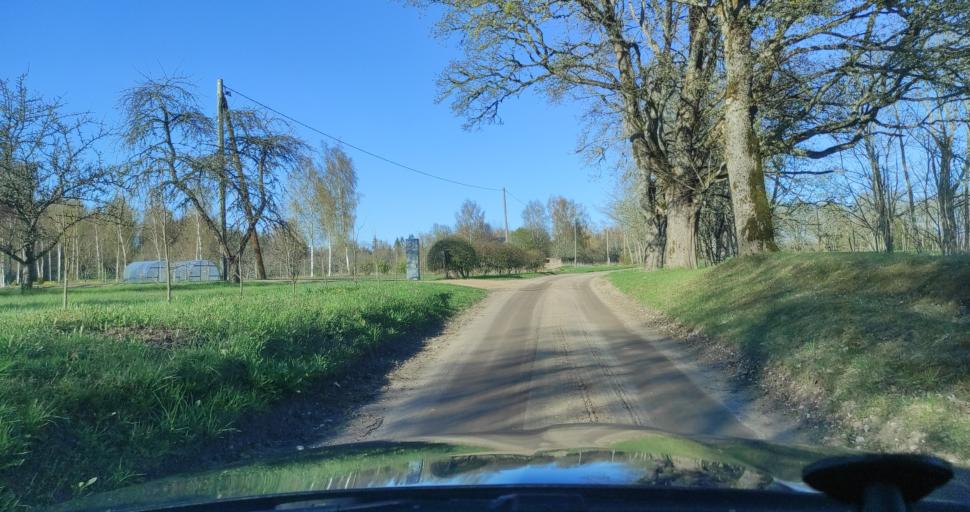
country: LV
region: Kuldigas Rajons
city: Kuldiga
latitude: 56.8692
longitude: 21.8465
